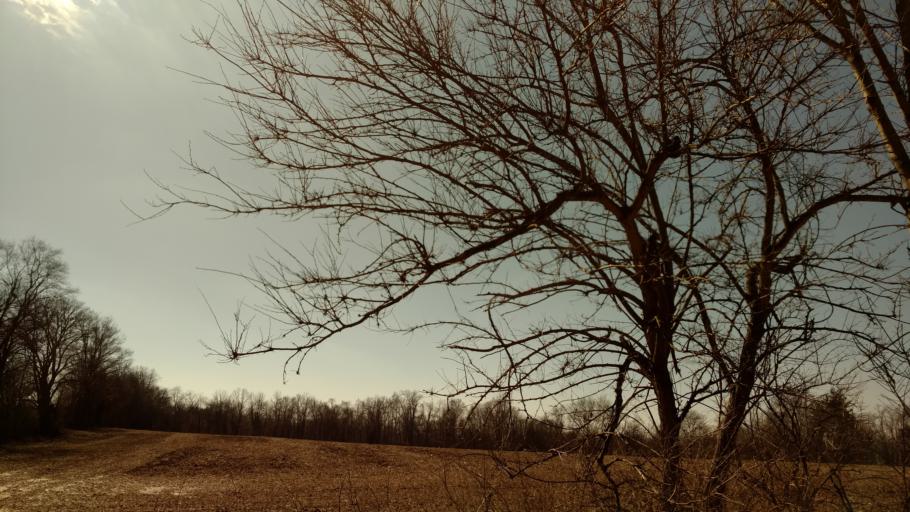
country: US
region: Ohio
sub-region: Morrow County
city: Cardington
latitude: 40.4990
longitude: -82.8747
